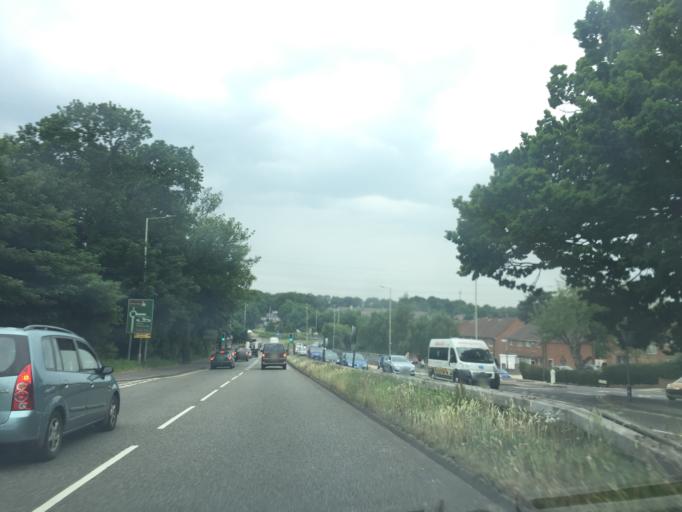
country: GB
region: England
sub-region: Dorset
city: Parkstone
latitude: 50.7526
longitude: -1.9341
